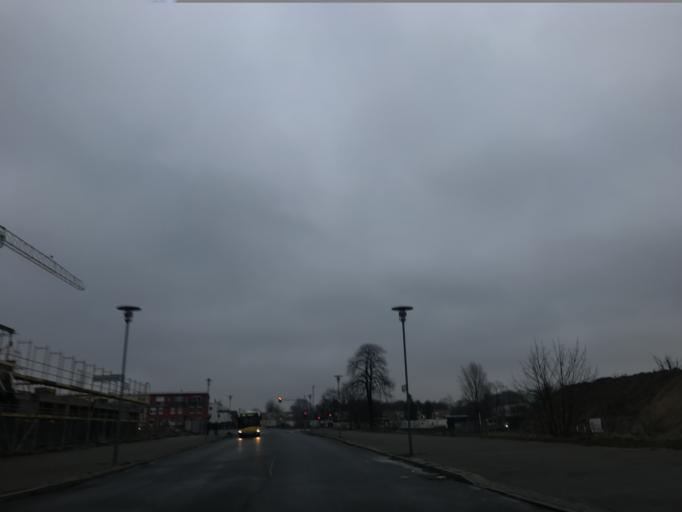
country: DE
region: Berlin
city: Hakenfelde
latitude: 52.5555
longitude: 13.2231
